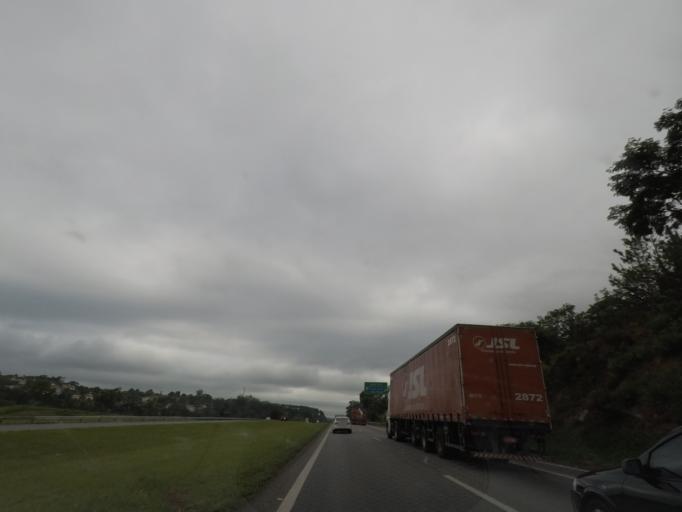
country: BR
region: Sao Paulo
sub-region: Atibaia
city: Atibaia
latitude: -23.1008
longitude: -46.5743
